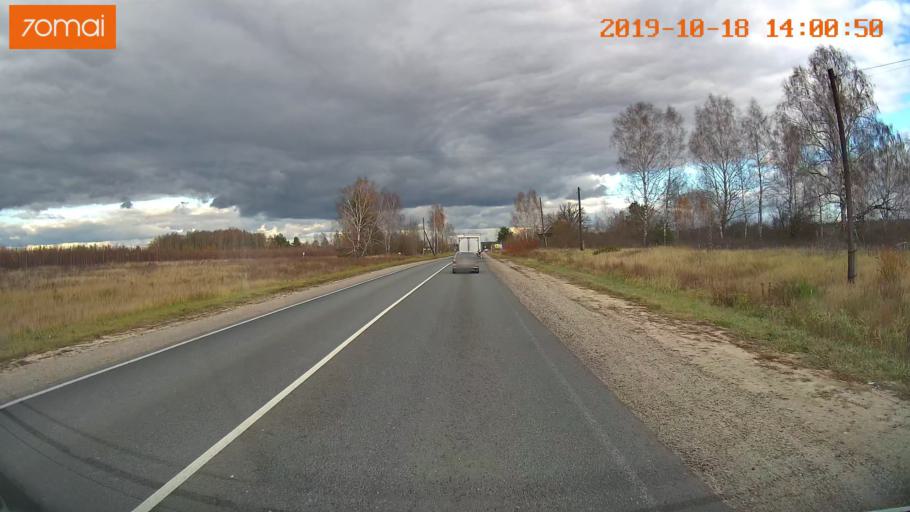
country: RU
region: Rjazan
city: Spas-Klepiki
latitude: 55.1035
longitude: 40.0810
